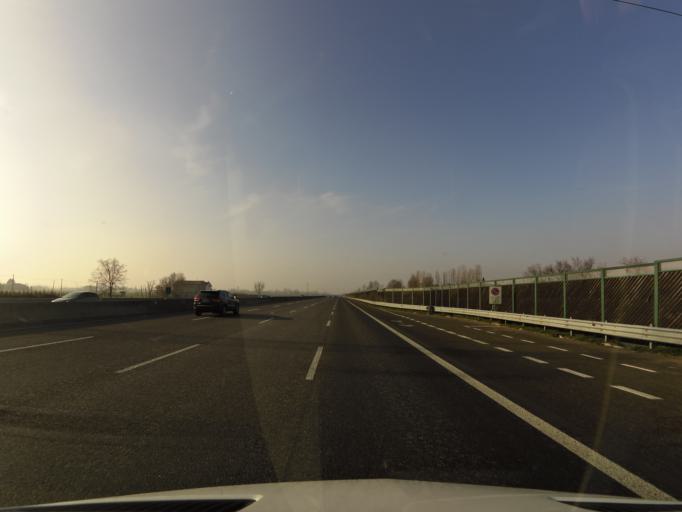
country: IT
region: Emilia-Romagna
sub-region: Provincia di Modena
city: San Damaso
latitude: 44.5913
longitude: 10.9487
